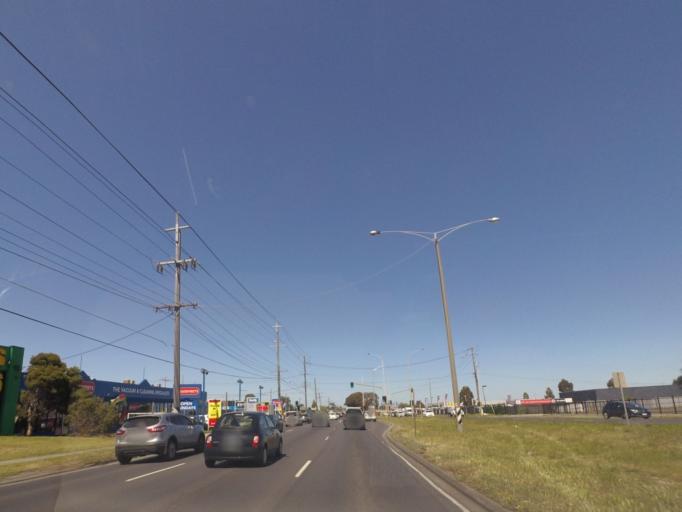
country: AU
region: Victoria
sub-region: Hume
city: Campbellfield
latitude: -37.6778
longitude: 144.9565
